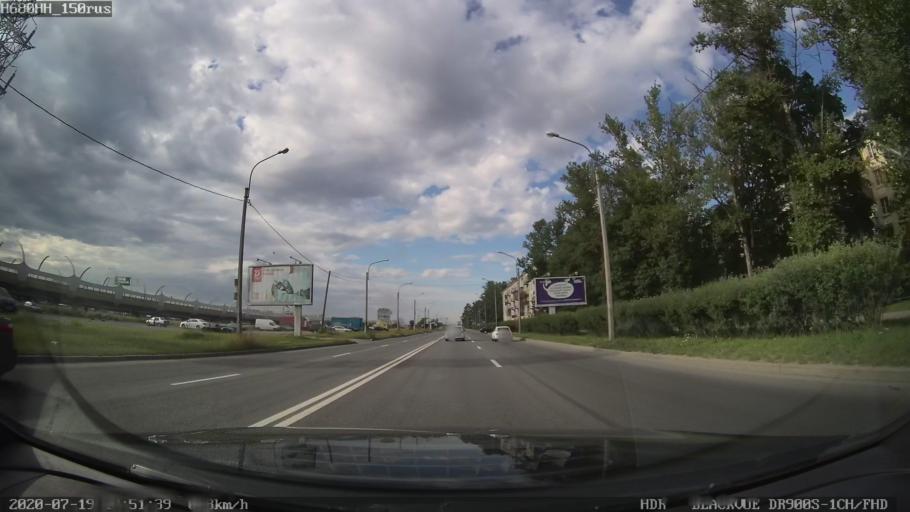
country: RU
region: St.-Petersburg
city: Avtovo
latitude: 59.8591
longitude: 30.2943
